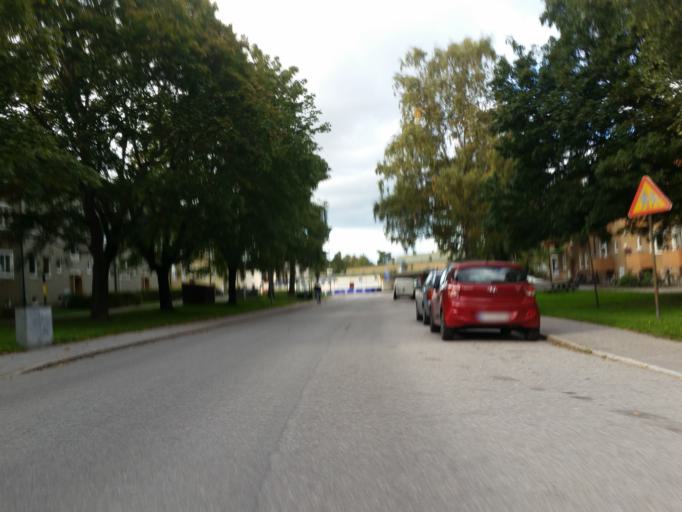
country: SE
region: Stockholm
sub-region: Stockholms Kommun
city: OEstermalm
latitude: 59.2865
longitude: 18.1091
